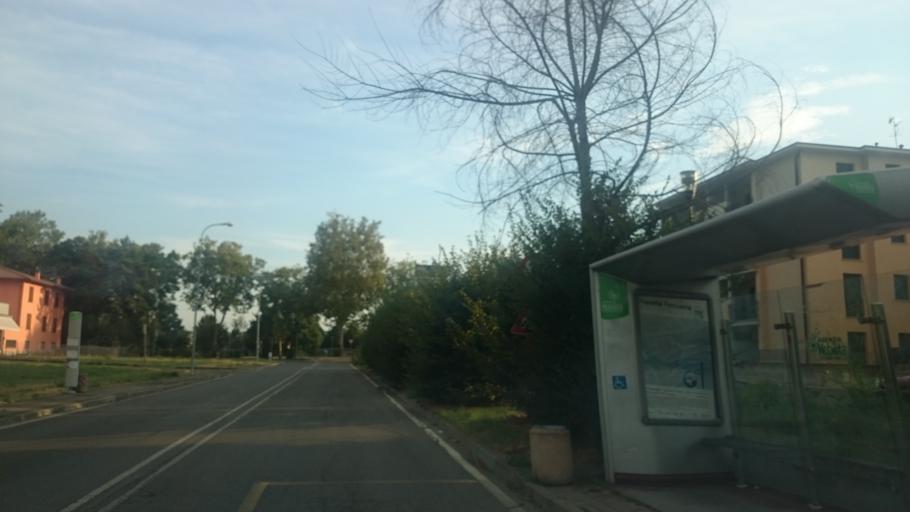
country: IT
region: Emilia-Romagna
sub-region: Provincia di Reggio Emilia
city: Reggio nell'Emilia
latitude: 44.7037
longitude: 10.6563
